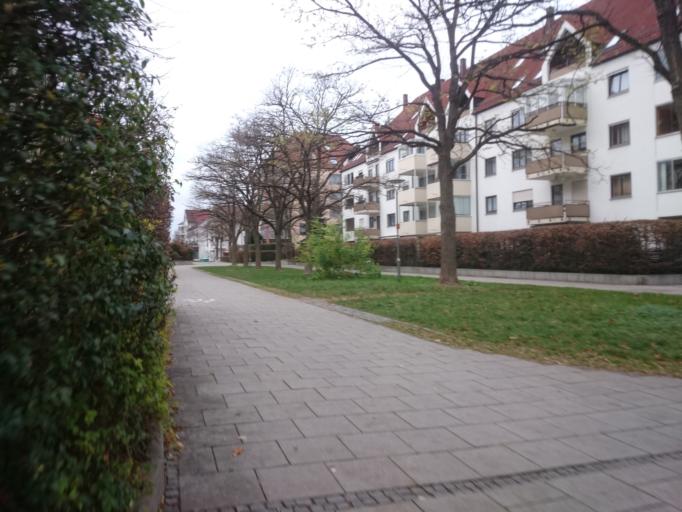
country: DE
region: Bavaria
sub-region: Swabia
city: Augsburg
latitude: 48.3317
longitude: 10.9008
